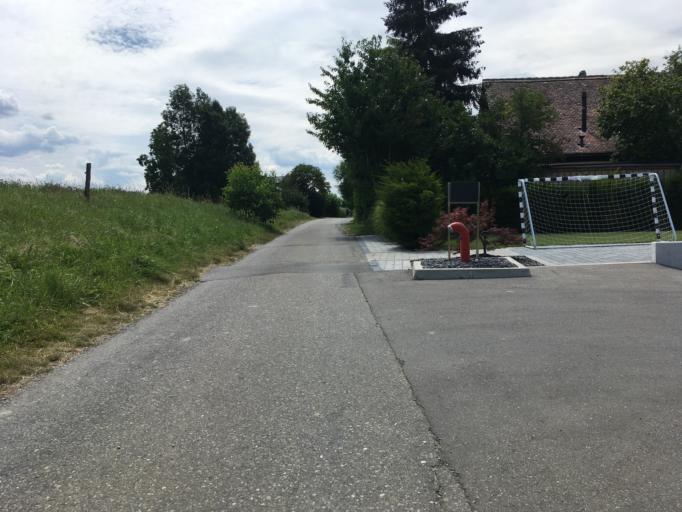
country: CH
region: Vaud
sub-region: Broye-Vully District
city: Payerne
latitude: 46.8892
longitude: 6.9122
